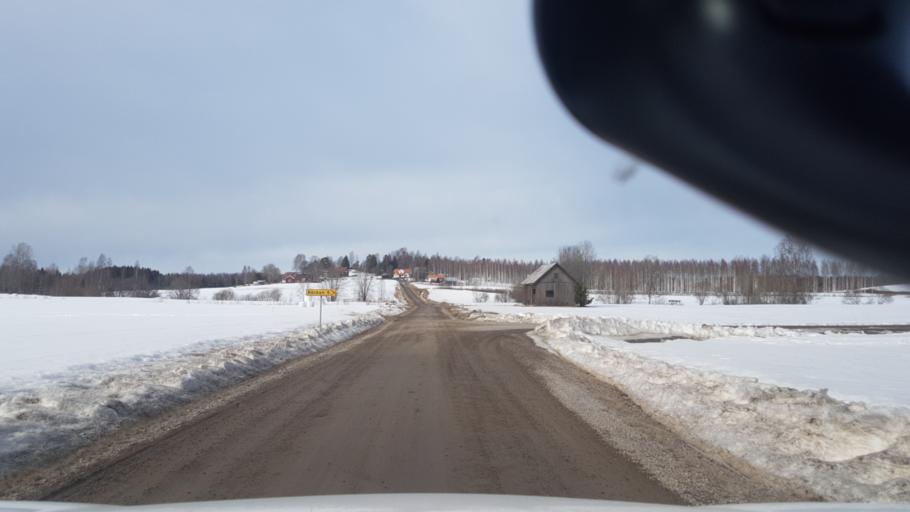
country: SE
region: Vaermland
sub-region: Eda Kommun
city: Charlottenberg
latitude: 59.8448
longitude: 12.3498
